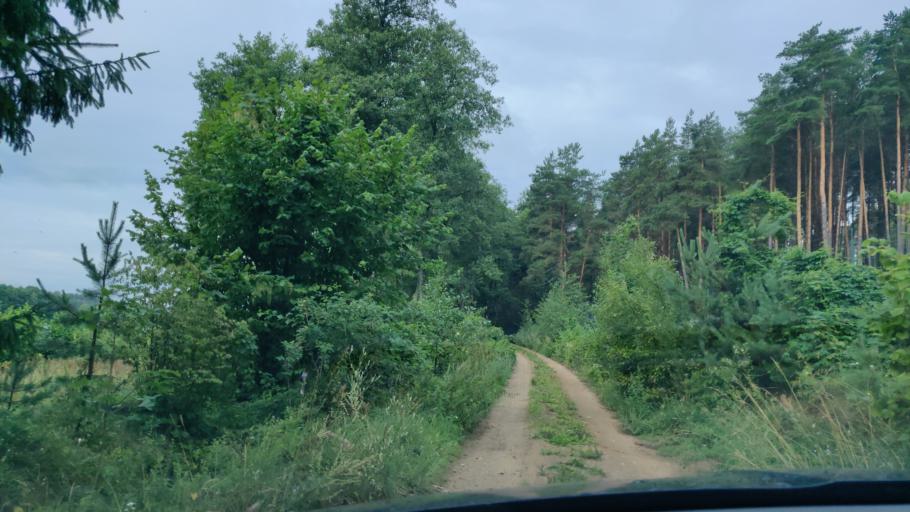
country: LT
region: Vilnius County
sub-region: Trakai
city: Rudiskes
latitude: 54.6097
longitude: 24.8324
